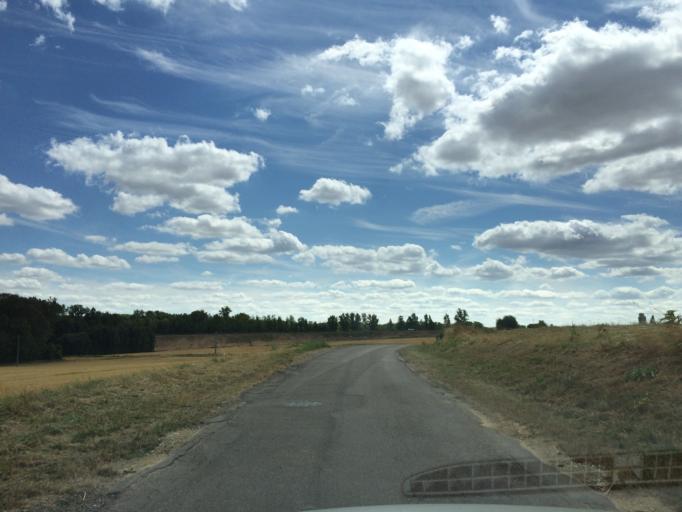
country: FR
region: Bourgogne
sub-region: Departement de l'Yonne
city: Fleury-la-Vallee
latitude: 47.8901
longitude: 3.4241
